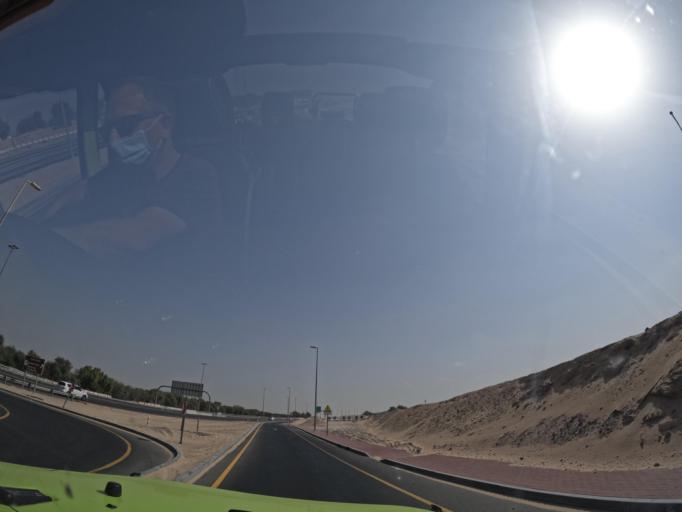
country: AE
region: Ash Shariqah
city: Sharjah
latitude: 25.2054
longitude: 55.4329
